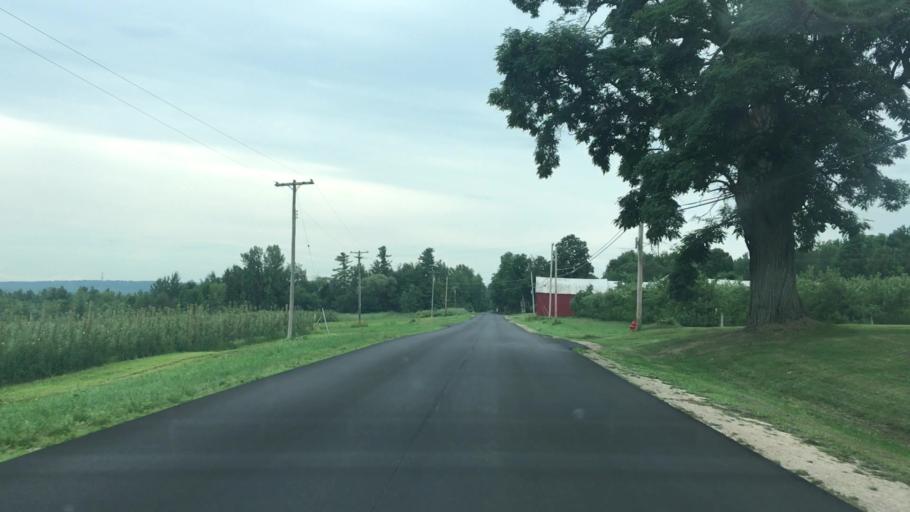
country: US
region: New York
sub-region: Clinton County
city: Peru
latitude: 44.5676
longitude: -73.5701
